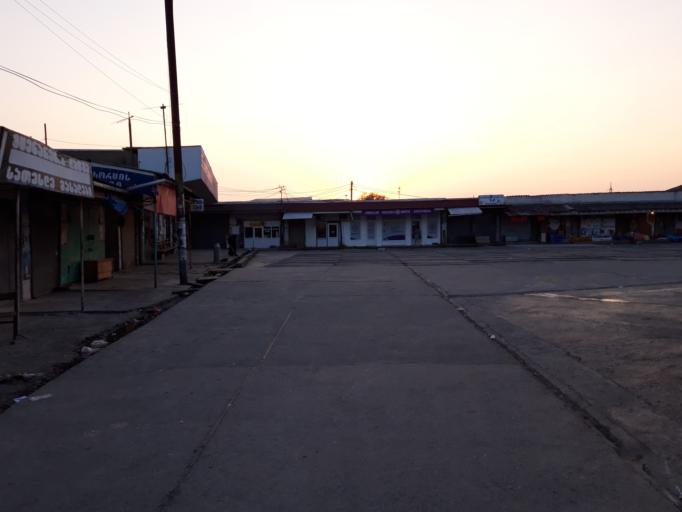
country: GE
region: Imereti
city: Samtredia
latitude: 42.1668
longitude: 42.3416
